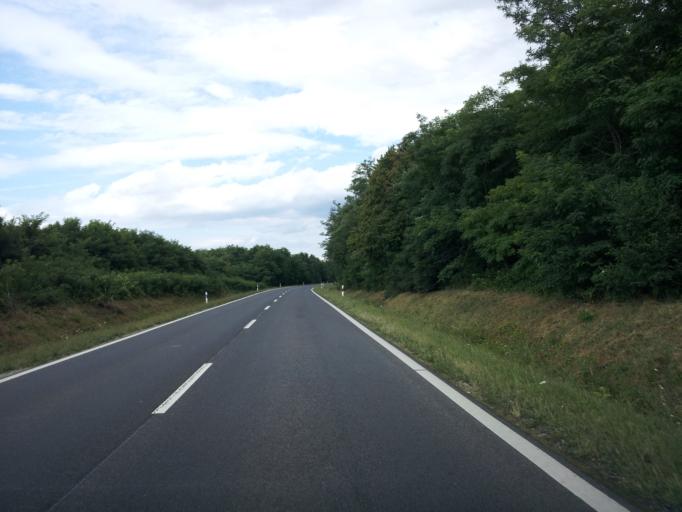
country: HU
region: Vas
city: Janoshaza
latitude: 47.1109
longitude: 17.0993
